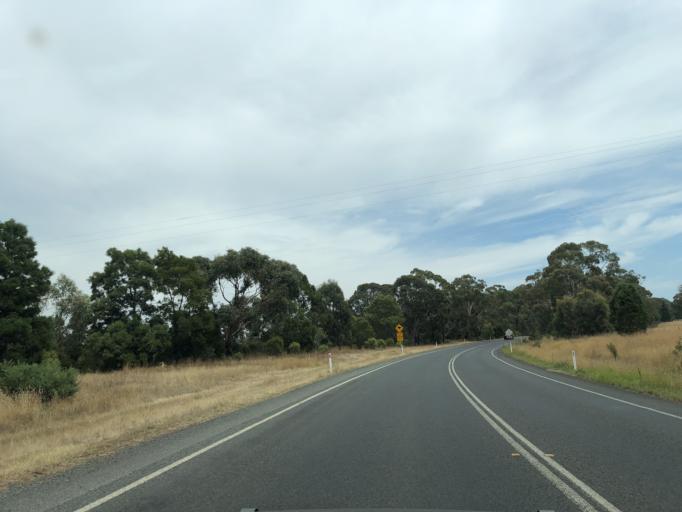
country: AU
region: Victoria
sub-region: Hume
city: Sunbury
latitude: -37.4902
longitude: 144.5680
